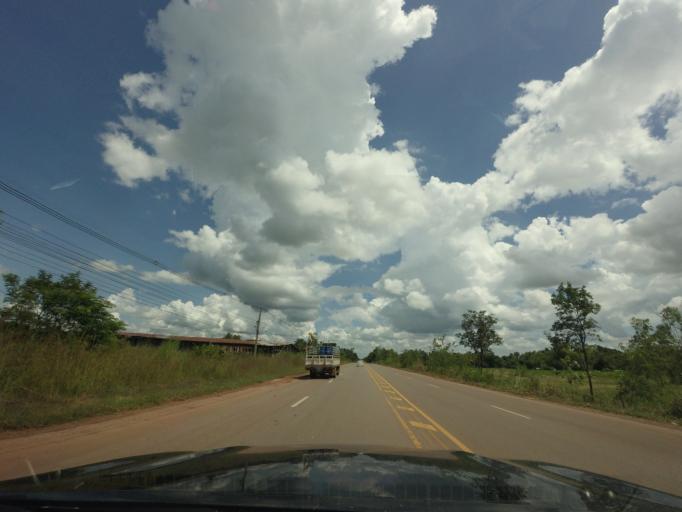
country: TH
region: Changwat Udon Thani
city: Ban Dung
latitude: 17.6818
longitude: 103.2244
